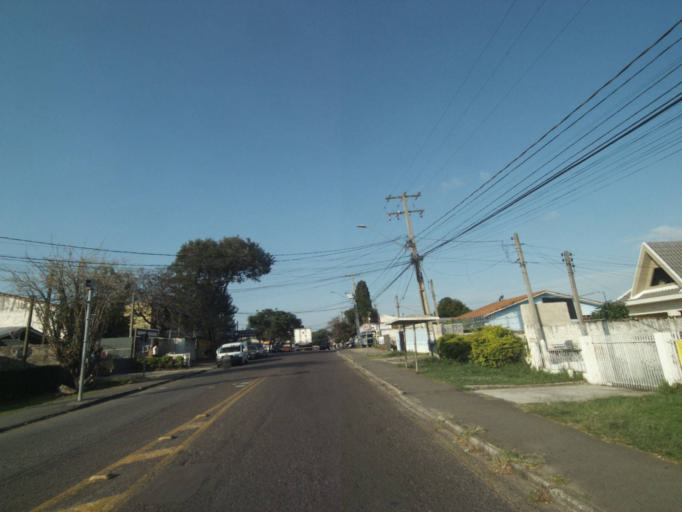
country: BR
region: Parana
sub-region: Curitiba
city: Curitiba
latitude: -25.4831
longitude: -49.3315
